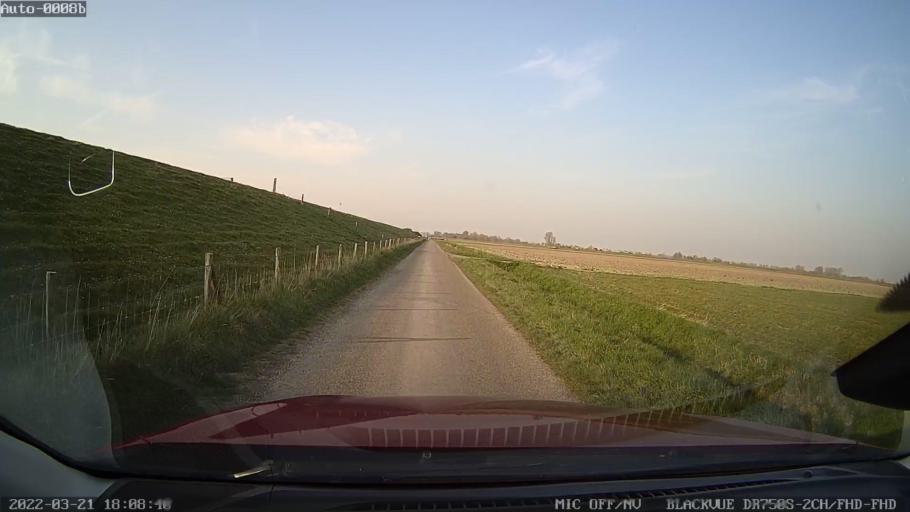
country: NL
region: North Brabant
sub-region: Gemeente Steenbergen
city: Nieuw-Vossemeer
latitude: 51.5640
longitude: 4.2348
